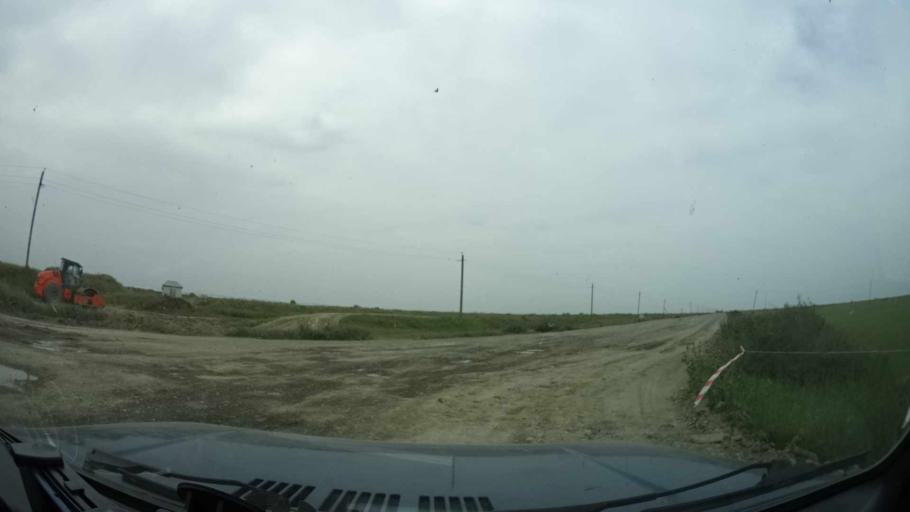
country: IR
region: Ardabil
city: Bileh Savar
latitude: 39.6156
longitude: 48.2157
